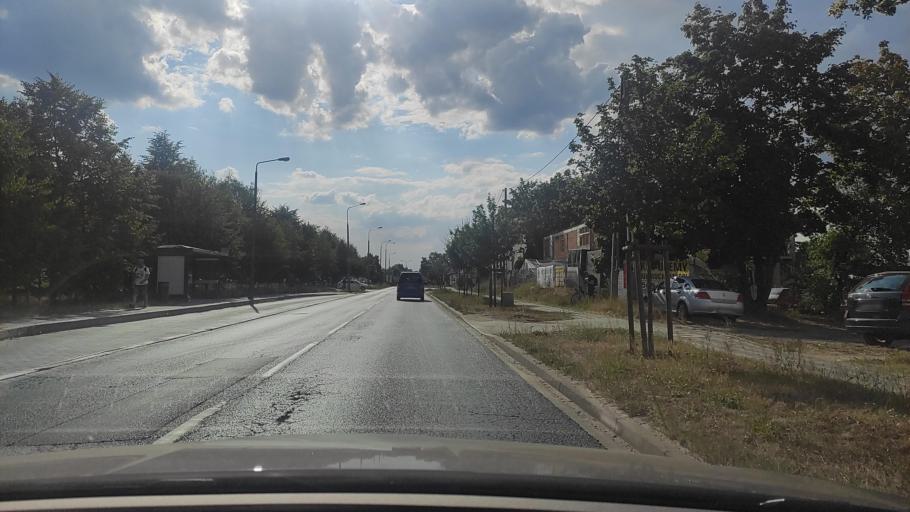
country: PL
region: Greater Poland Voivodeship
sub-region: Poznan
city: Poznan
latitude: 52.4196
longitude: 16.9665
